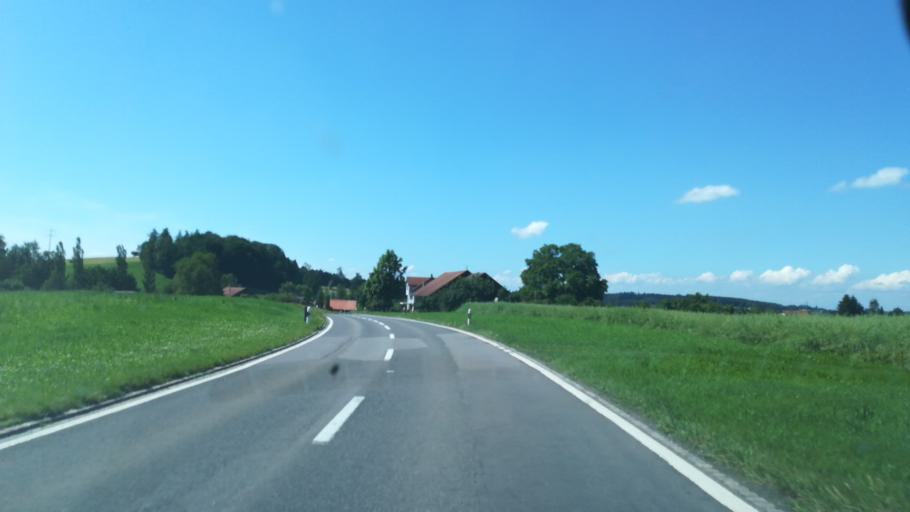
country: CH
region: Saint Gallen
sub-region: Wahlkreis St. Gallen
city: Andwil
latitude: 47.4570
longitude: 9.2513
